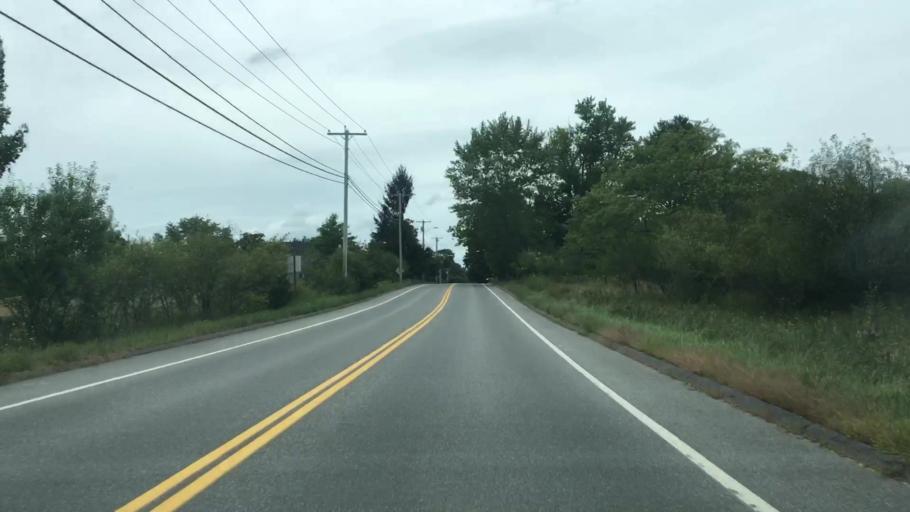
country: US
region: Maine
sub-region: Cumberland County
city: Yarmouth
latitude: 43.8260
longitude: -70.1933
